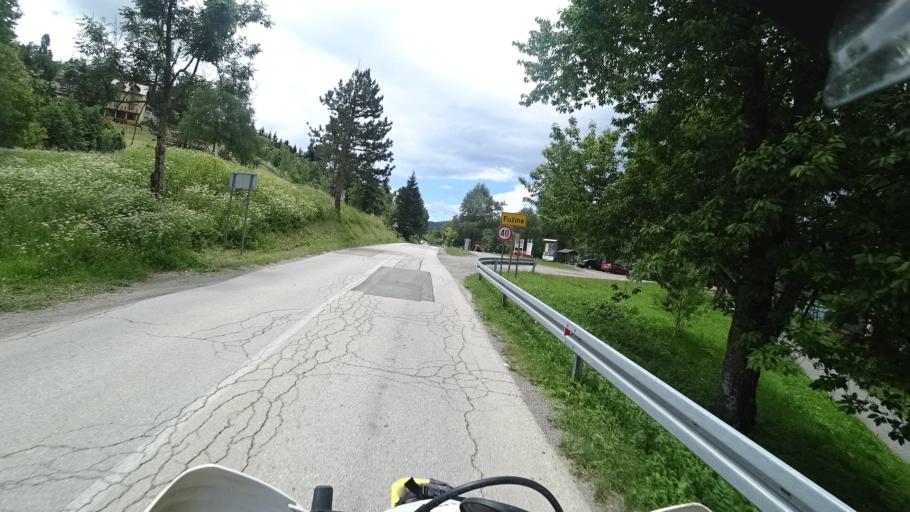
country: HR
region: Primorsko-Goranska
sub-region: Grad Delnice
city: Delnice
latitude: 45.3127
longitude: 14.7176
